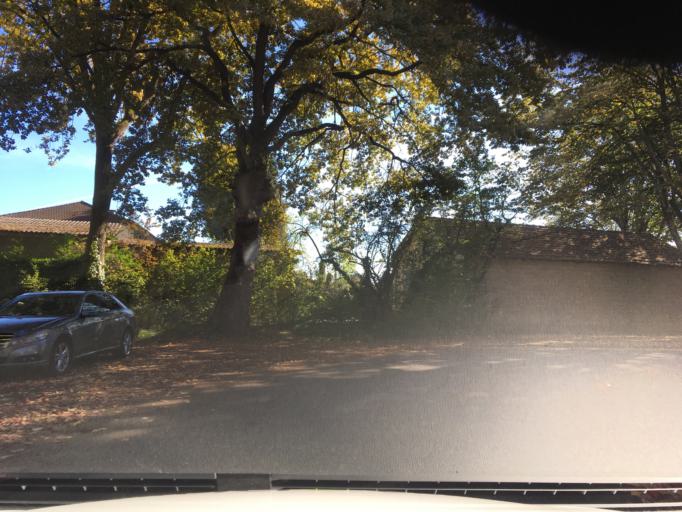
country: FR
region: Aquitaine
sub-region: Departement des Pyrenees-Atlantiques
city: Pau
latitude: 43.3152
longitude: -0.3425
